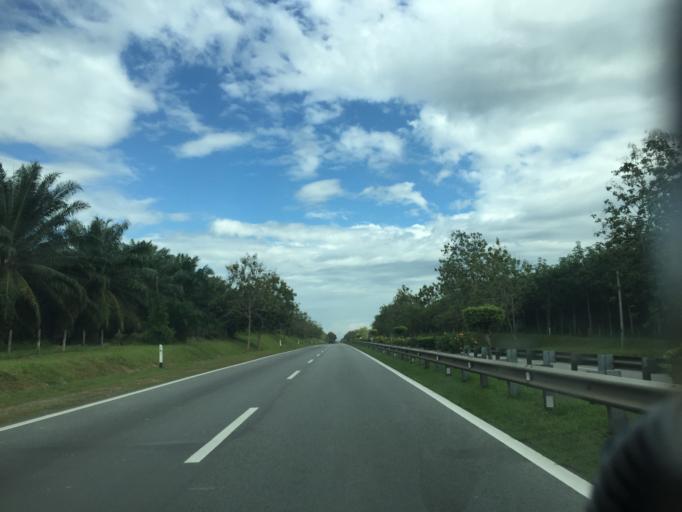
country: MY
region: Kedah
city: Jitra
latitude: 6.3745
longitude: 100.4238
